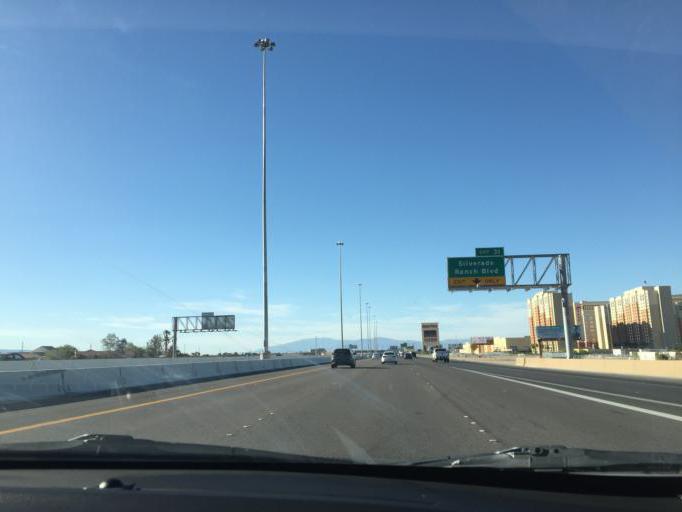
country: US
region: Nevada
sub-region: Clark County
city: Enterprise
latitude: 36.0032
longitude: -115.1804
